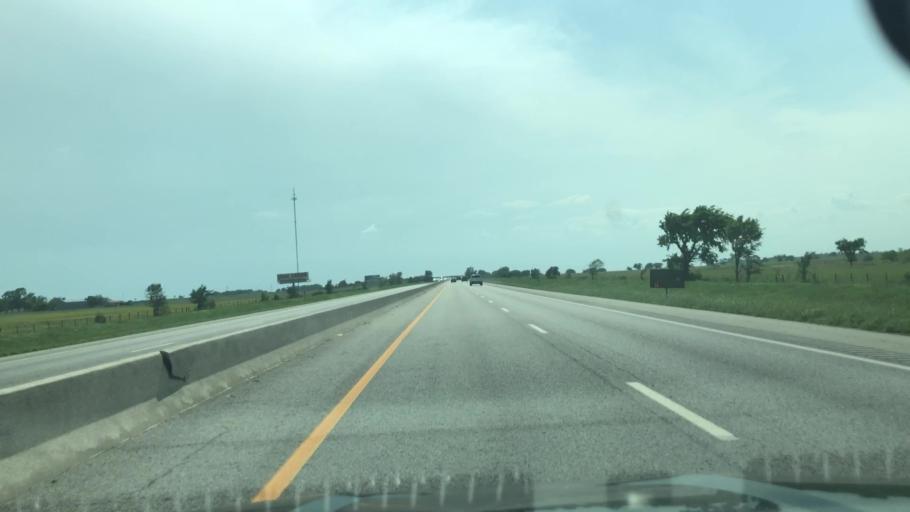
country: US
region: Oklahoma
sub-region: Ottawa County
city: Afton
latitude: 36.7045
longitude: -94.9847
